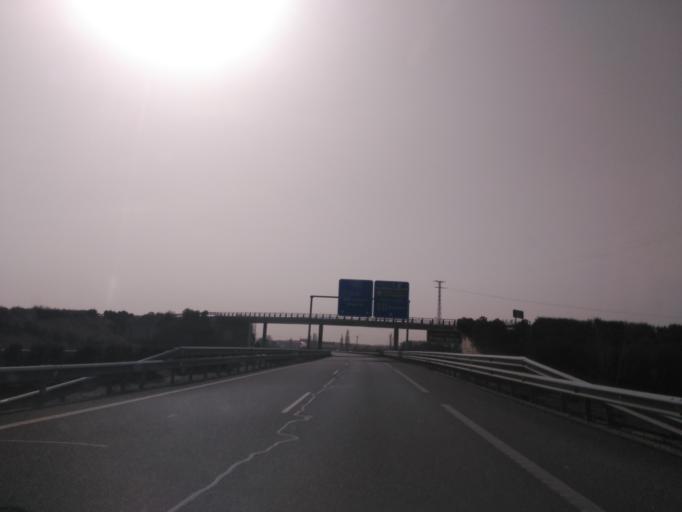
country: ES
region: Castille and Leon
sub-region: Provincia de Palencia
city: Villamuriel de Cerrato
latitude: 41.9524
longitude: -4.5039
